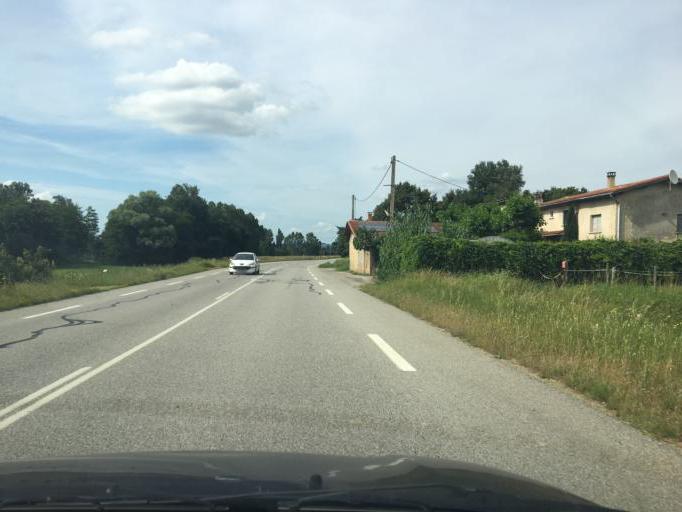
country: FR
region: Rhone-Alpes
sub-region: Departement de la Drome
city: Chanos-Curson
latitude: 45.0655
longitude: 4.9321
